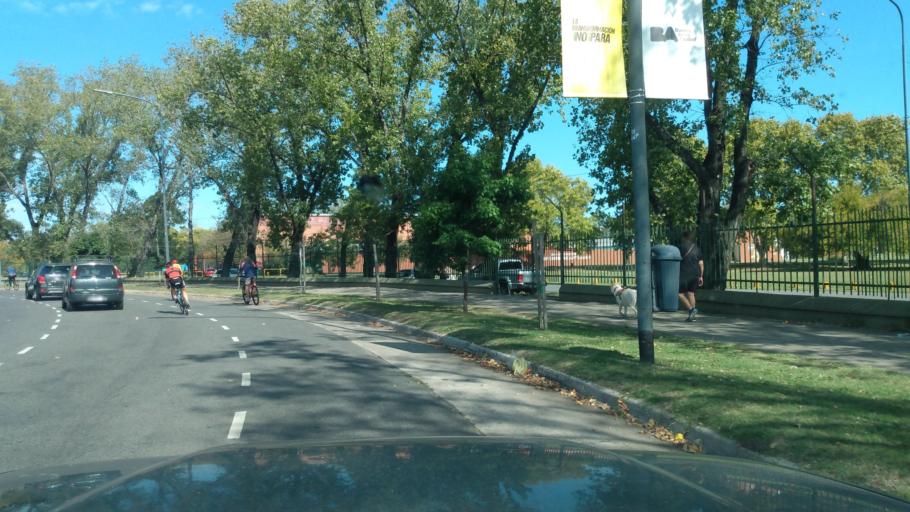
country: AR
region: Buenos Aires
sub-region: Partido de General San Martin
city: General San Martin
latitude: -34.5566
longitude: -58.4969
